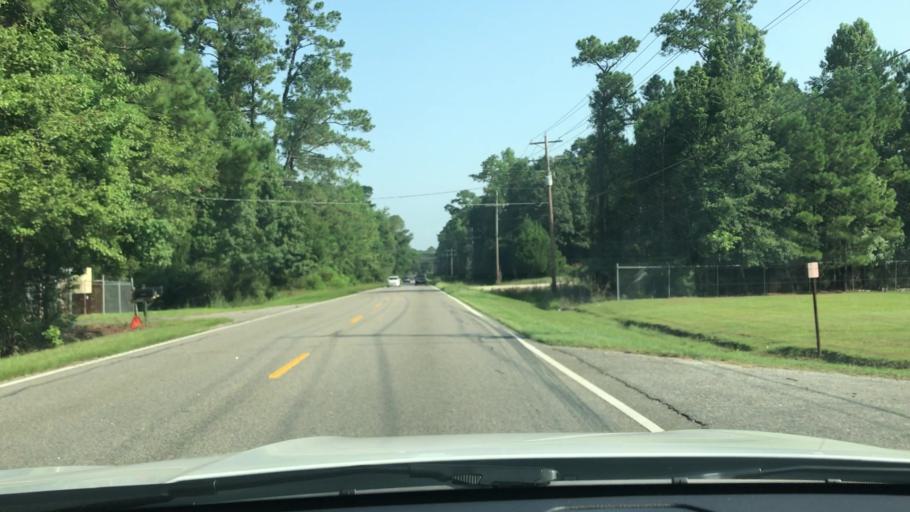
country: US
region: South Carolina
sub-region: Georgetown County
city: Georgetown
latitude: 33.4521
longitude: -79.2797
